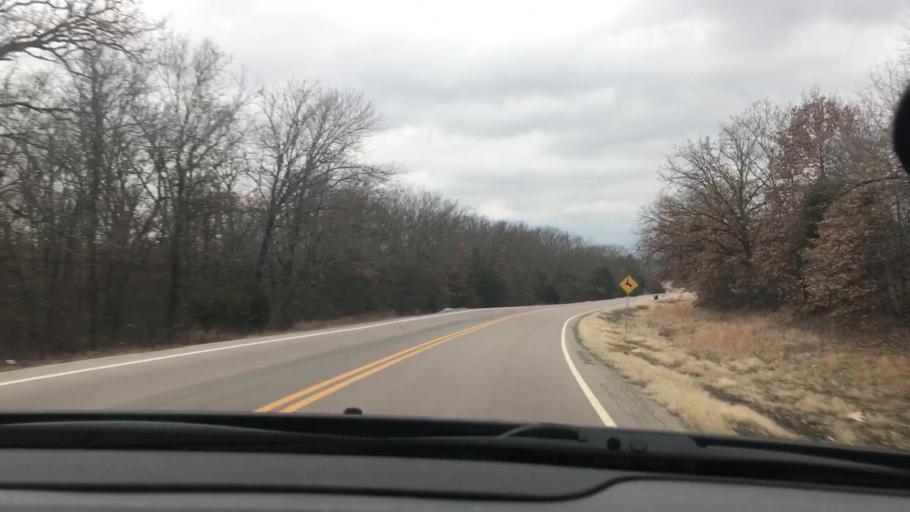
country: US
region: Oklahoma
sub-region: Coal County
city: Coalgate
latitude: 34.3704
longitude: -96.3849
